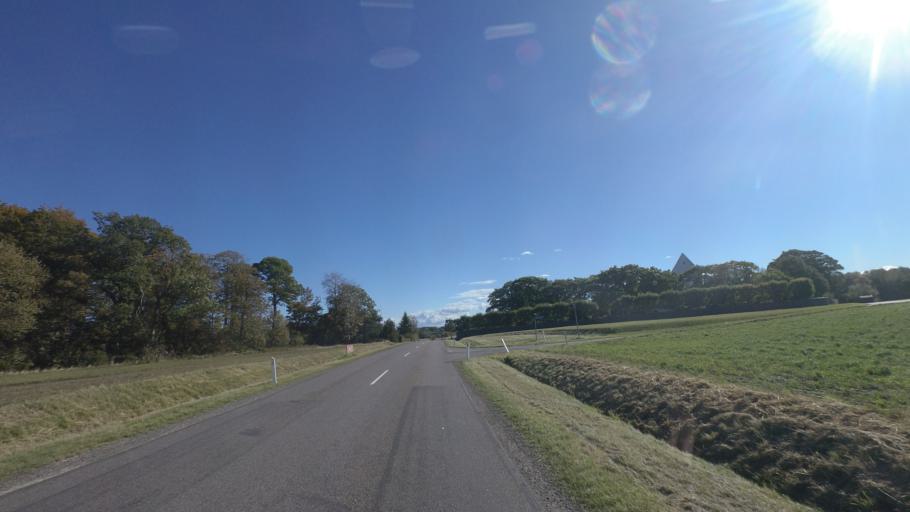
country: DK
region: Capital Region
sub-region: Bornholm Kommune
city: Nexo
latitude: 55.1185
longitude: 15.1049
